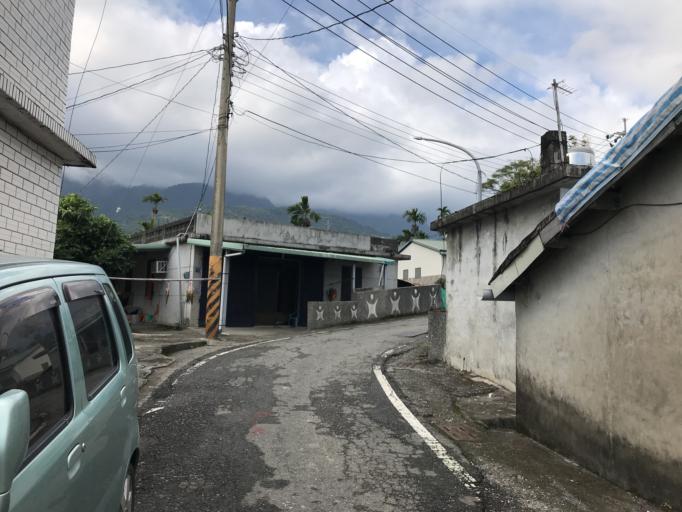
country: TW
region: Taiwan
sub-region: Taitung
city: Taitung
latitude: 23.1926
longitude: 121.3949
